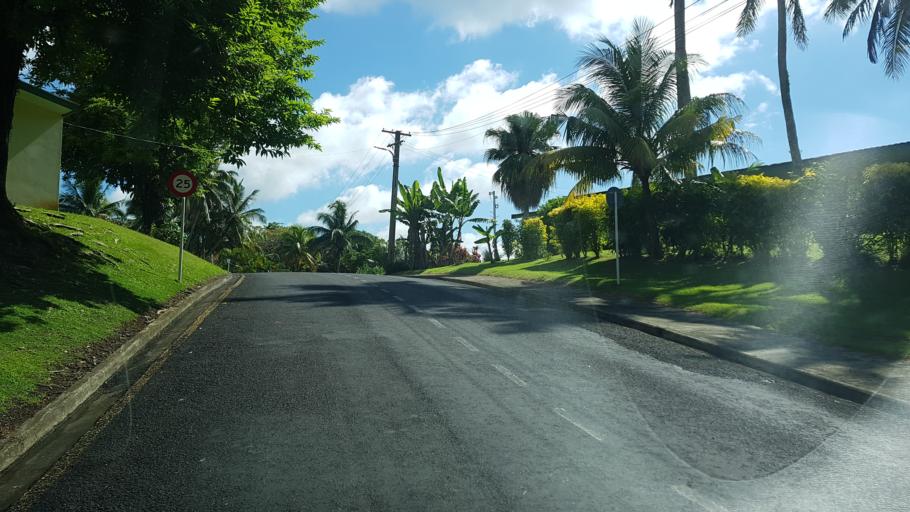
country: FJ
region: Central
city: Suva
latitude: -18.1535
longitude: 178.4433
